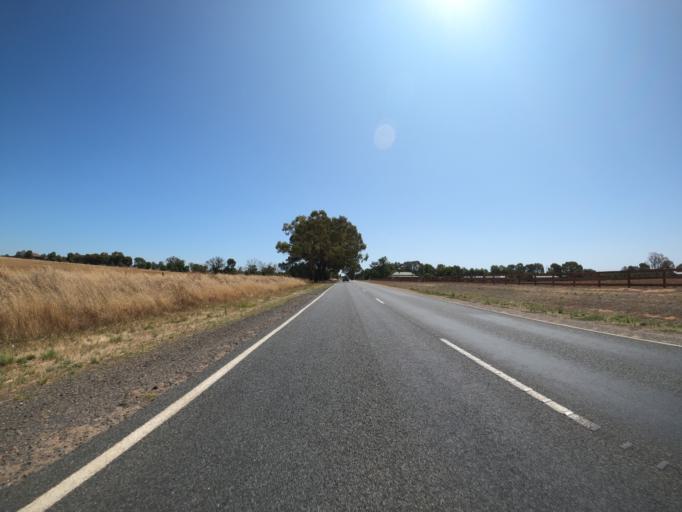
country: AU
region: Victoria
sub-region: Moira
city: Yarrawonga
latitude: -36.0257
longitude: 146.0960
